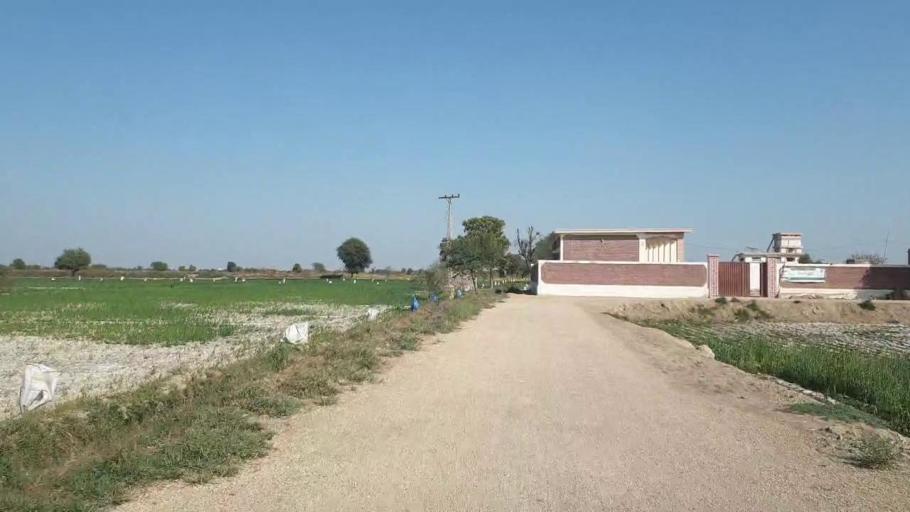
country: PK
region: Sindh
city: Tando Allahyar
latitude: 25.4069
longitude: 68.7063
